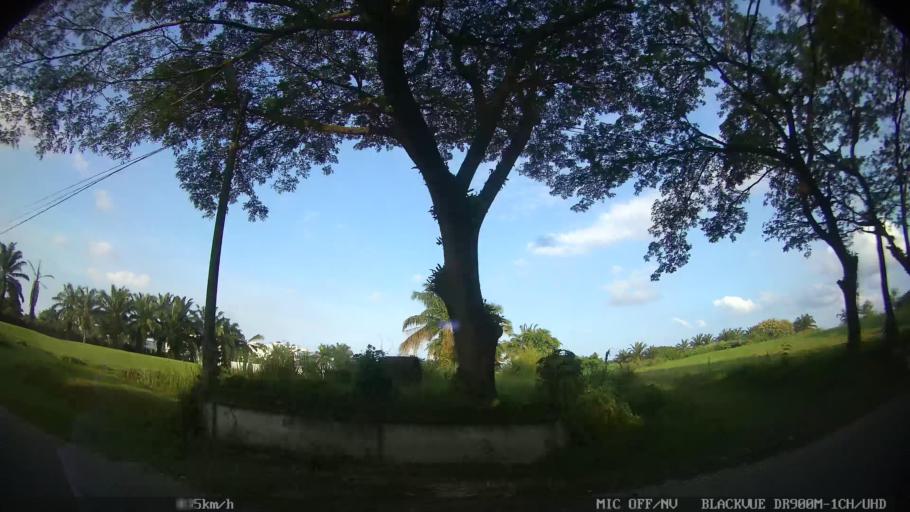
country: ID
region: North Sumatra
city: Medan
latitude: 3.6238
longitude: 98.6428
